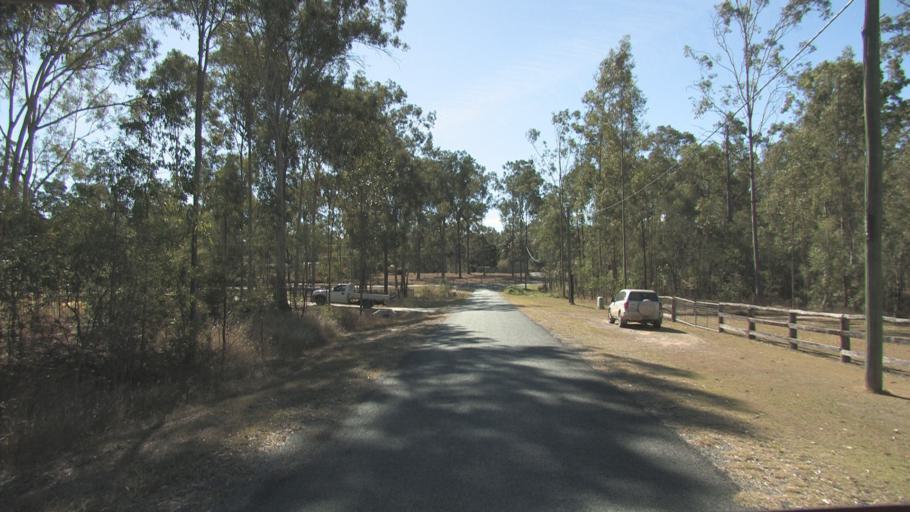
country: AU
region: Queensland
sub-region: Logan
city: North Maclean
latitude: -27.8218
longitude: 152.9815
